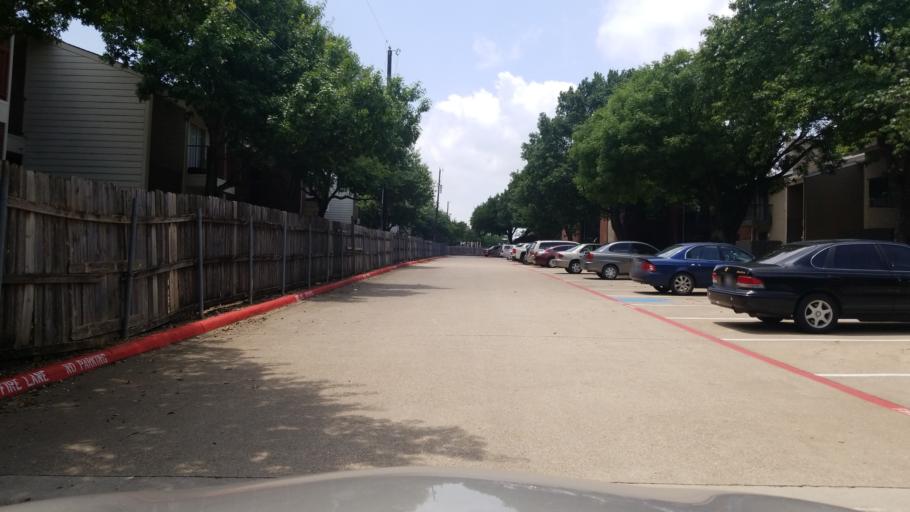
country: US
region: Texas
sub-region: Dallas County
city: Duncanville
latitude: 32.6863
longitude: -96.9091
